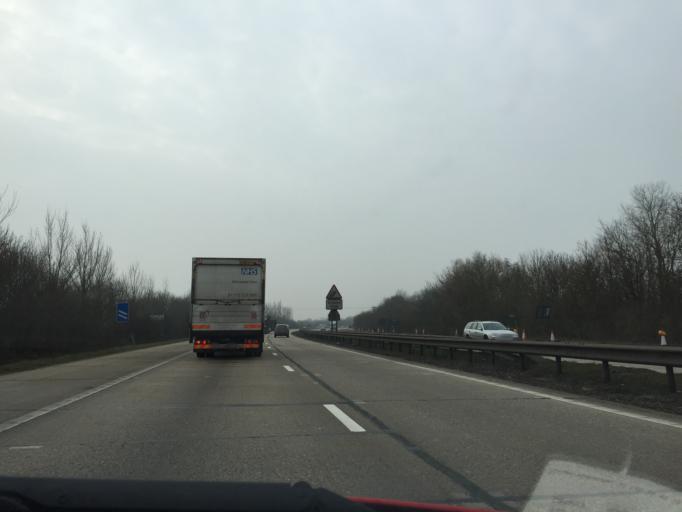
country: GB
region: England
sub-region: Hampshire
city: Totton
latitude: 50.9409
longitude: -1.4735
